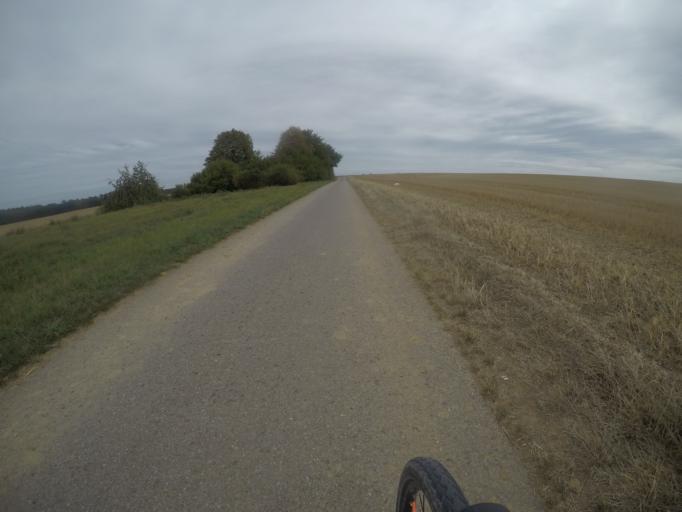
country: DE
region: Baden-Wuerttemberg
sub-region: Regierungsbezirk Stuttgart
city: Sersheim
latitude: 48.9479
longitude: 8.9907
